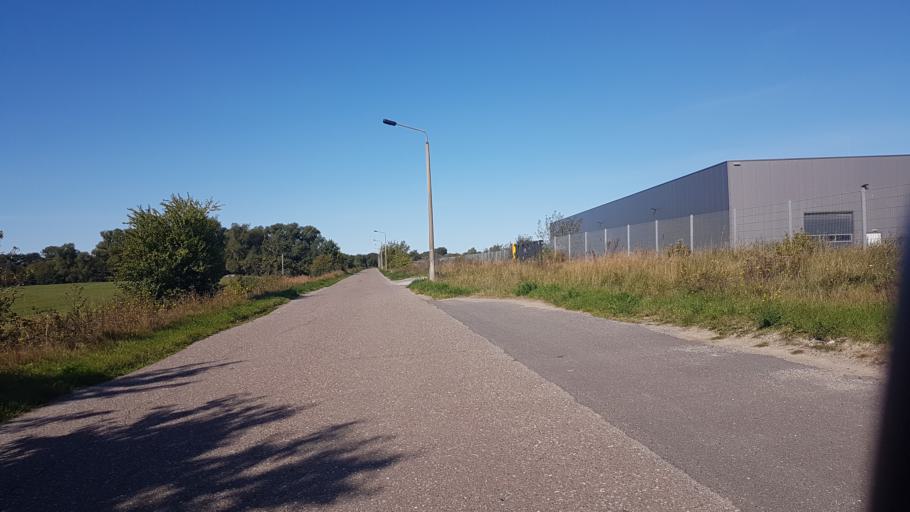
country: DE
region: Mecklenburg-Vorpommern
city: Sagard
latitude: 54.4935
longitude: 13.5608
